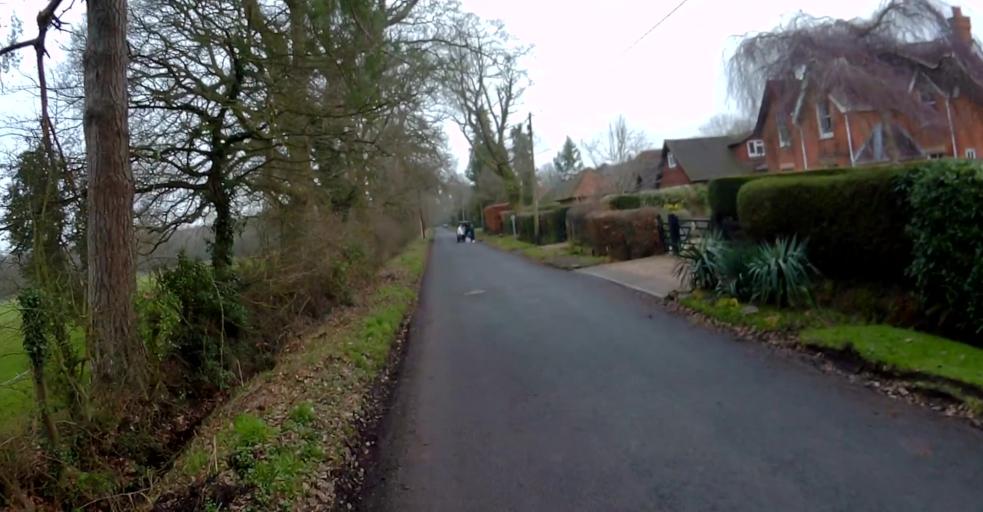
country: GB
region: England
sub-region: Hampshire
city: Eversley
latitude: 51.3557
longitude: -0.9047
